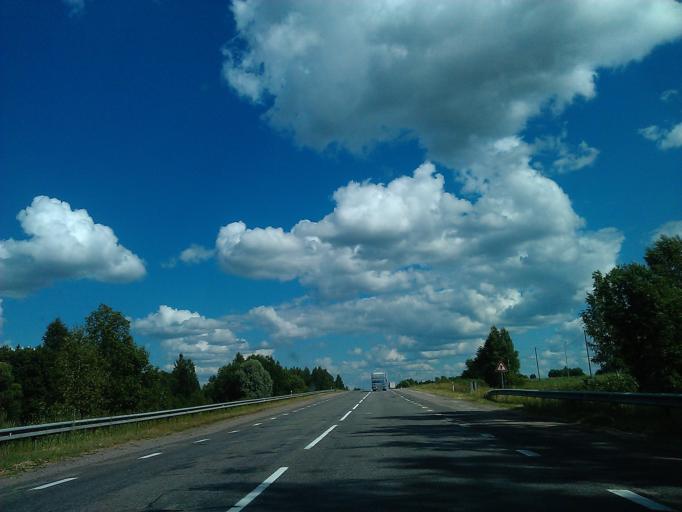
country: LV
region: Rezekne
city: Rezekne
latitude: 56.5483
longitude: 27.3365
